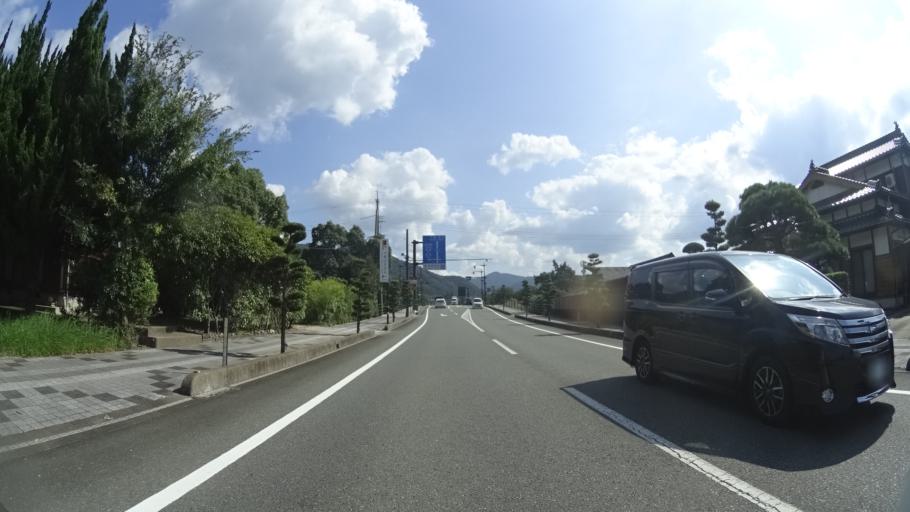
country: JP
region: Yamaguchi
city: Hagi
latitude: 34.4136
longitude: 131.4146
